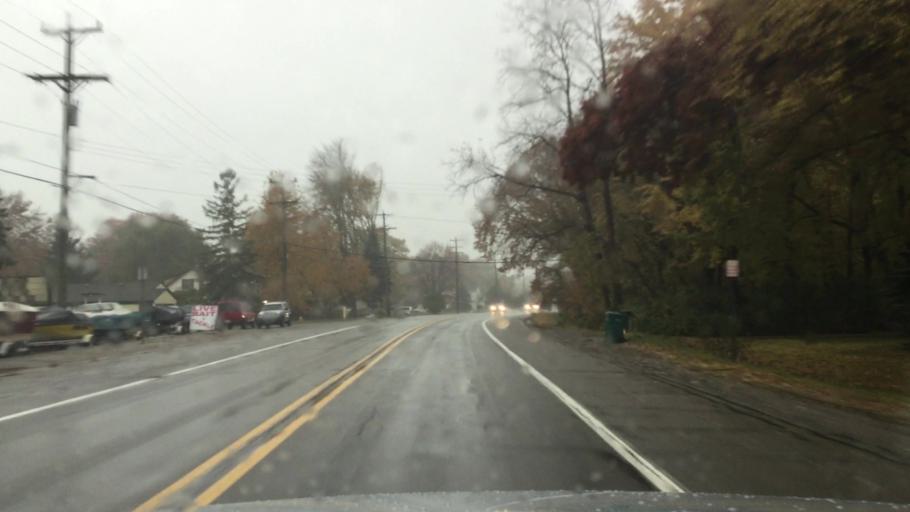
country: US
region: Michigan
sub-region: Macomb County
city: New Baltimore
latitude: 42.6875
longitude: -82.7125
